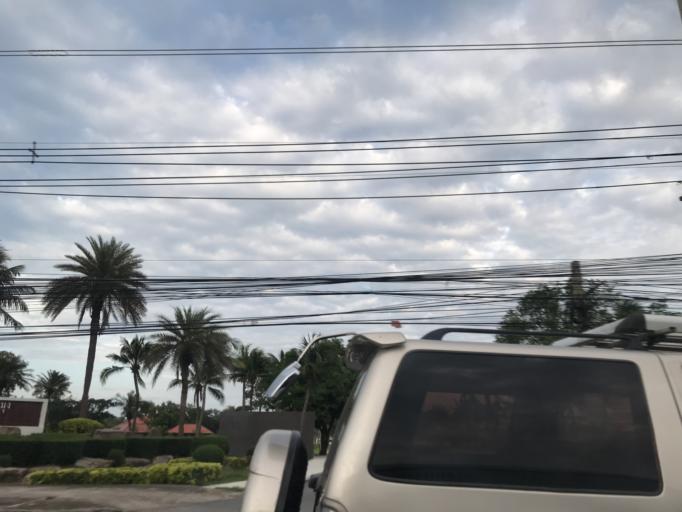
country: TH
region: Chon Buri
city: Bang Lamung
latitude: 13.0251
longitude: 100.9305
